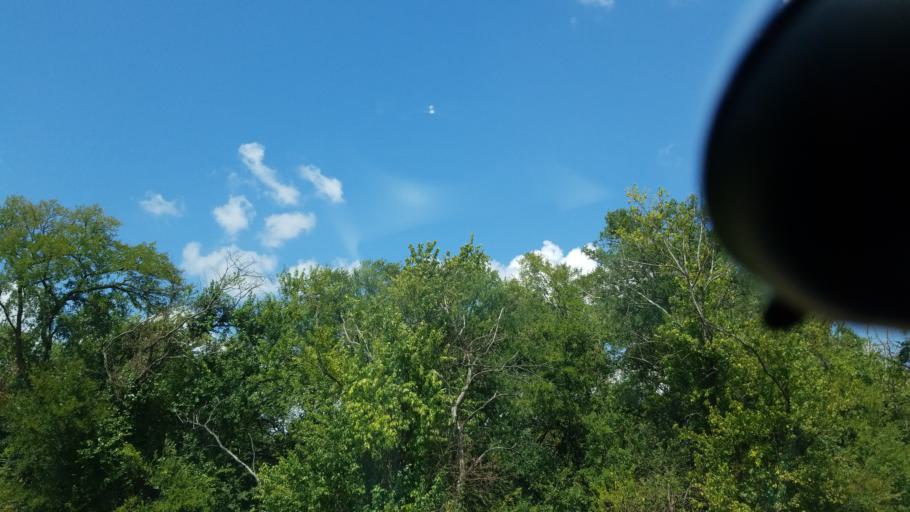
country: US
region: Texas
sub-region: Dallas County
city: Grand Prairie
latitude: 32.7260
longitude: -96.9893
